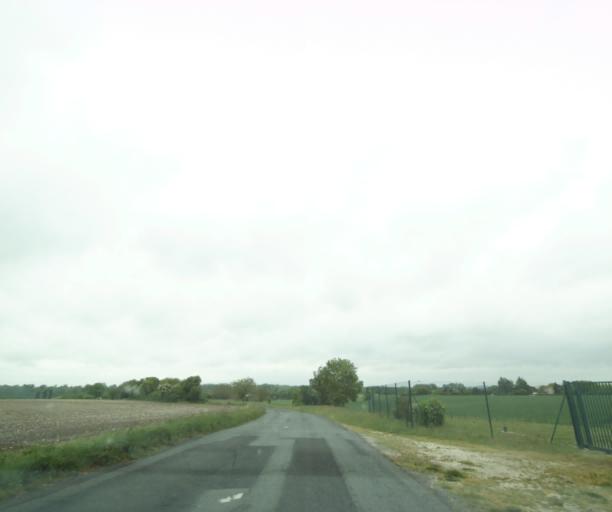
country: FR
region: Poitou-Charentes
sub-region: Departement de la Charente-Maritime
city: Pons
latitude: 45.6428
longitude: -0.5604
